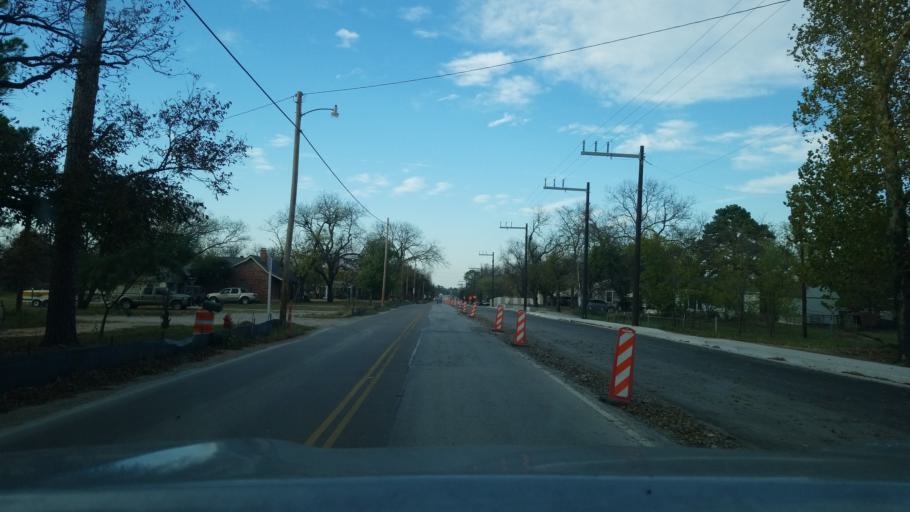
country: US
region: Texas
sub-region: Brown County
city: Lake Brownwood
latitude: 32.0894
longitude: -98.9640
